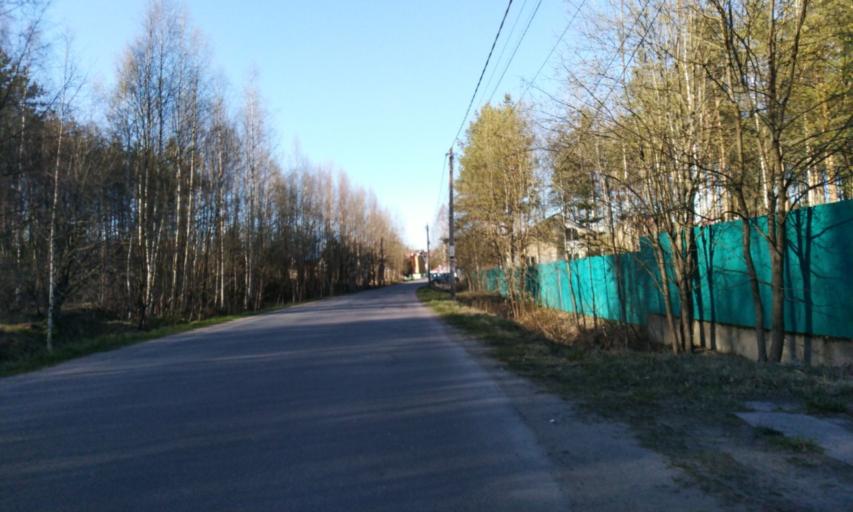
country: RU
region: Leningrad
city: Toksovo
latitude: 60.1426
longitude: 30.5554
